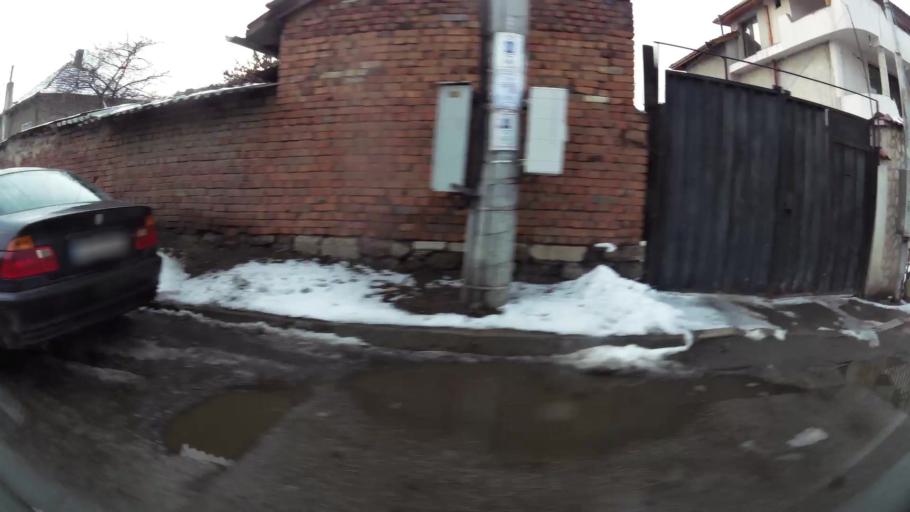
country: BG
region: Sofia-Capital
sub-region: Stolichna Obshtina
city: Sofia
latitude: 42.7250
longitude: 23.3468
